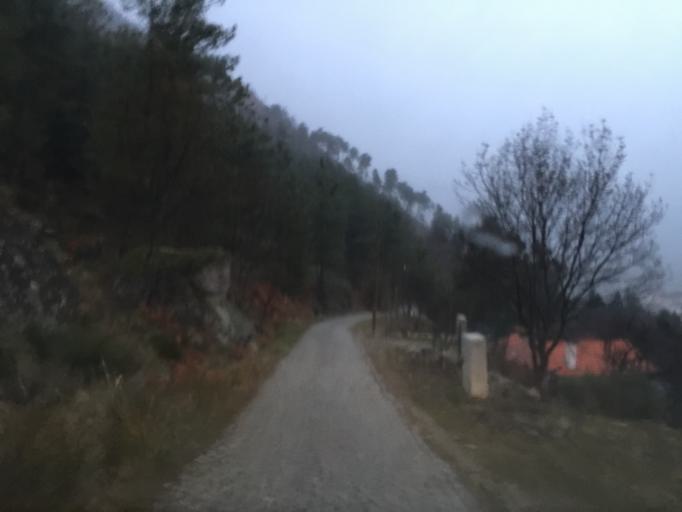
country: PT
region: Guarda
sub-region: Manteigas
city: Manteigas
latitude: 40.3825
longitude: -7.5480
